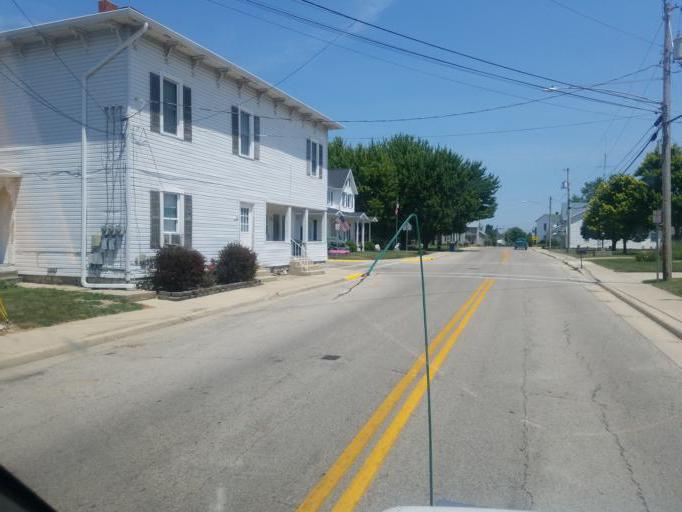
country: US
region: Ohio
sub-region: Shelby County
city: Fort Loramie
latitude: 40.3499
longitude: -84.3718
